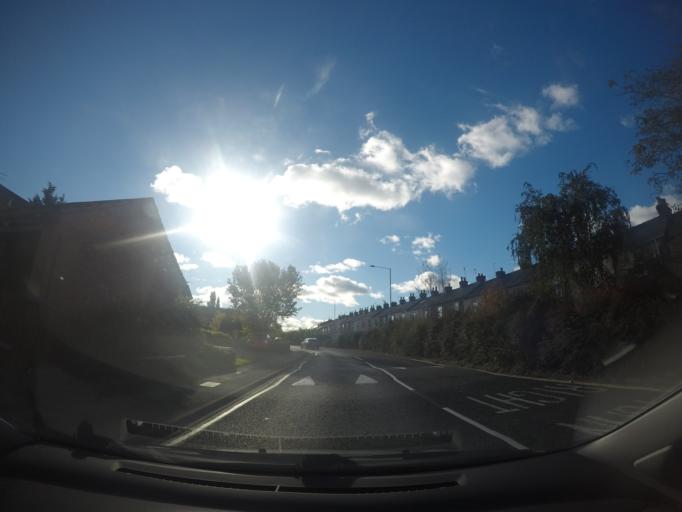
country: GB
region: England
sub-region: City of York
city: York
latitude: 53.9639
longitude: -1.1048
